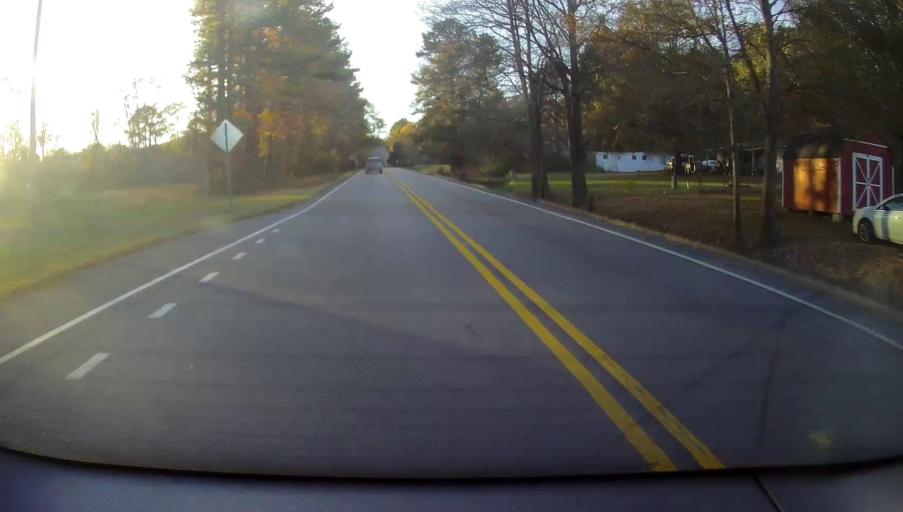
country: US
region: Alabama
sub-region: Saint Clair County
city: Steele
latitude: 34.0678
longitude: -86.3060
